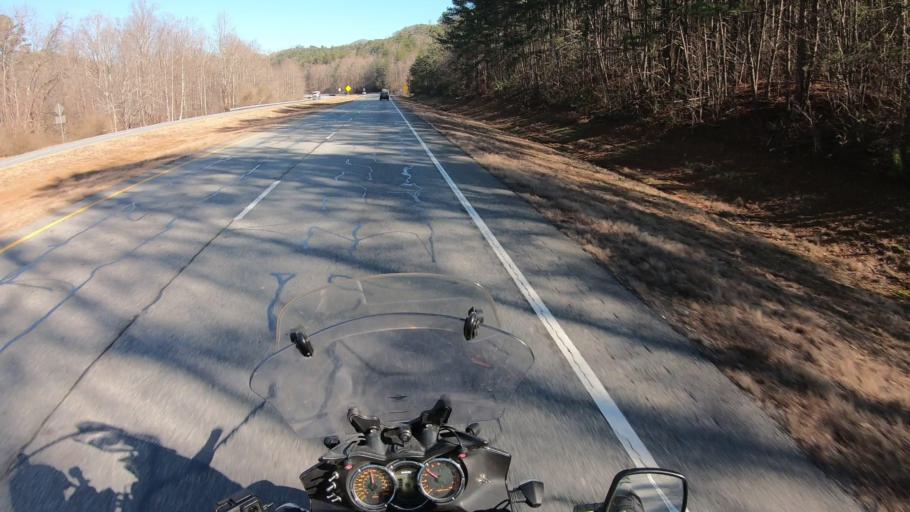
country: US
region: Georgia
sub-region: Gilmer County
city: Ellijay
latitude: 34.7254
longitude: -84.4407
